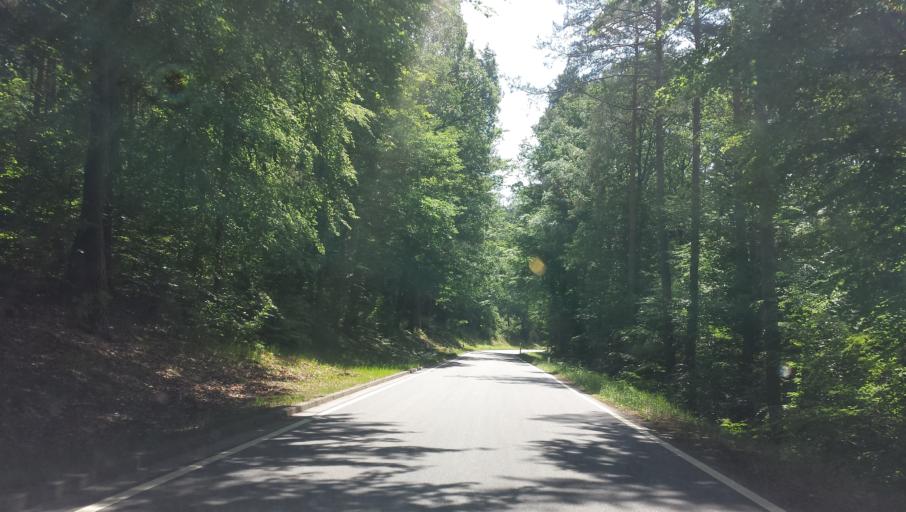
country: DE
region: Hesse
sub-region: Regierungsbezirk Darmstadt
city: Rothenberg
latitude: 49.5278
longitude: 8.9381
